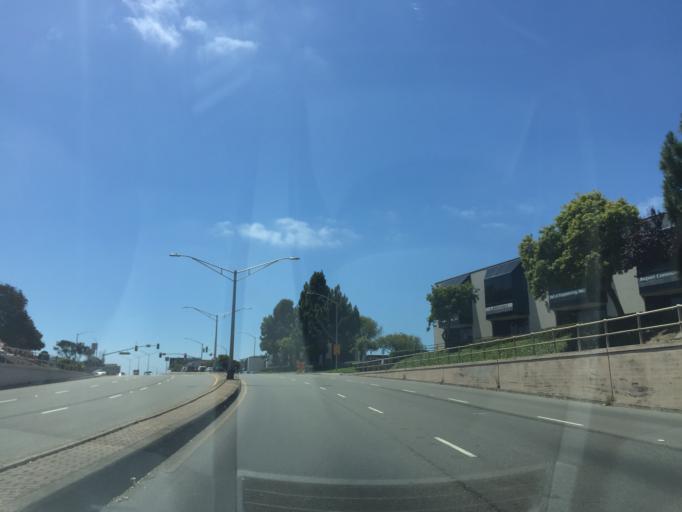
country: US
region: California
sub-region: San Mateo County
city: South San Francisco
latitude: 37.6510
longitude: -122.4089
